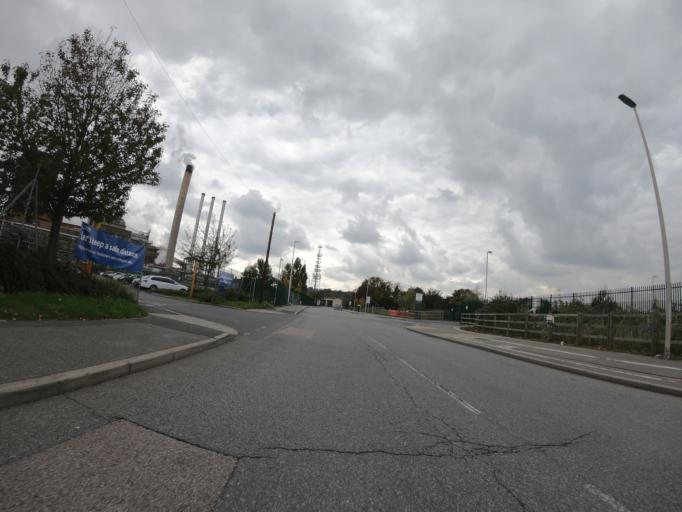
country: GB
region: England
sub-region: Greater London
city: Erith
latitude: 51.4949
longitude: 0.1679
